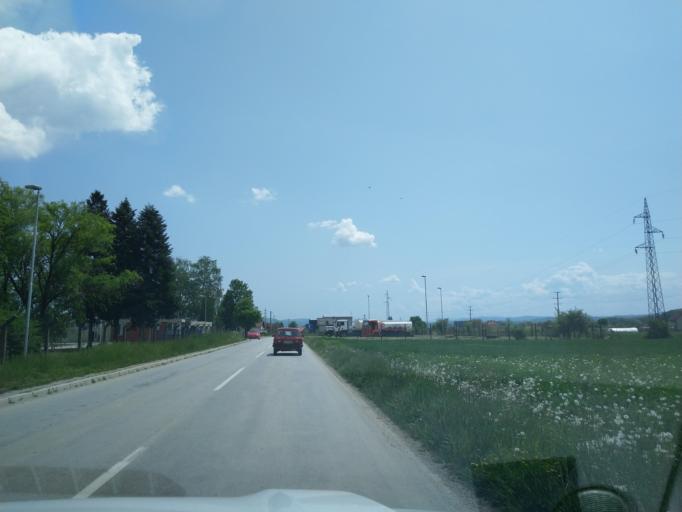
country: RS
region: Central Serbia
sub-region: Zlatiborski Okrug
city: Pozega
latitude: 43.8490
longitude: 20.0108
